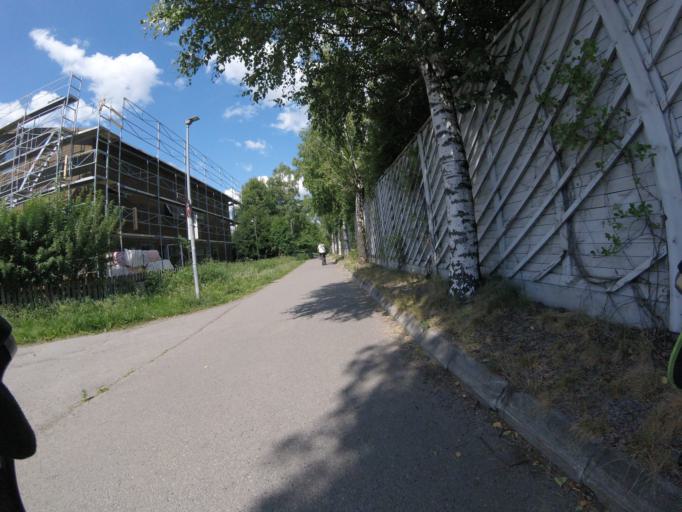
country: NO
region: Akershus
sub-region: Skedsmo
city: Lillestrom
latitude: 59.9601
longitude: 11.0649
